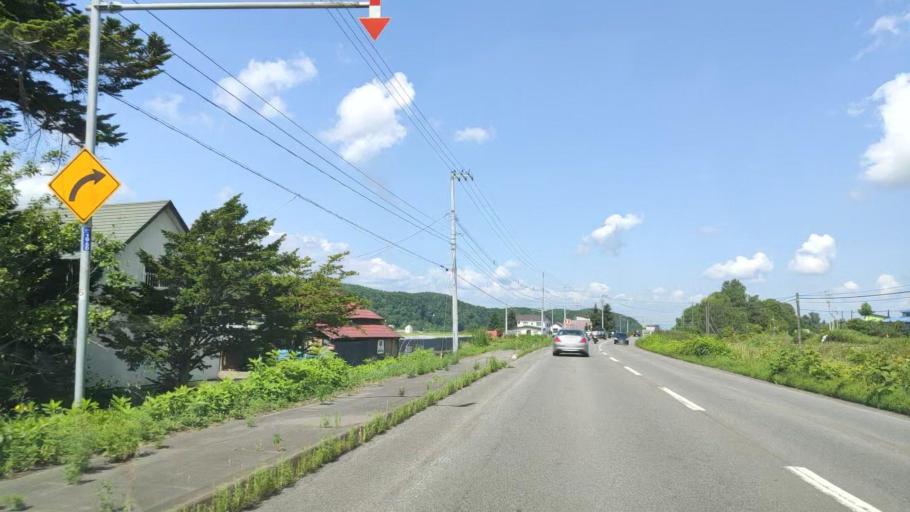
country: JP
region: Hokkaido
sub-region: Asahikawa-shi
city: Asahikawa
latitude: 43.6314
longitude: 142.4599
